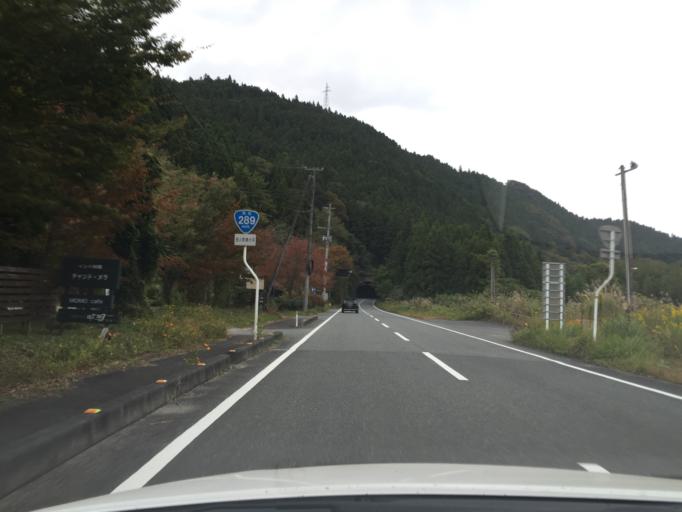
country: JP
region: Ibaraki
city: Kitaibaraki
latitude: 36.9201
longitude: 140.7062
